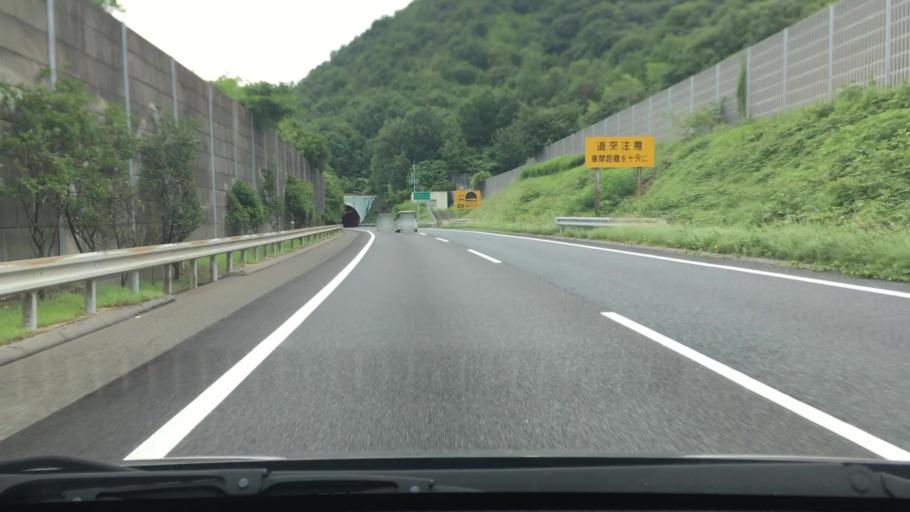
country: JP
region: Hiroshima
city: Ono-hara
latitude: 34.2632
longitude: 132.2320
